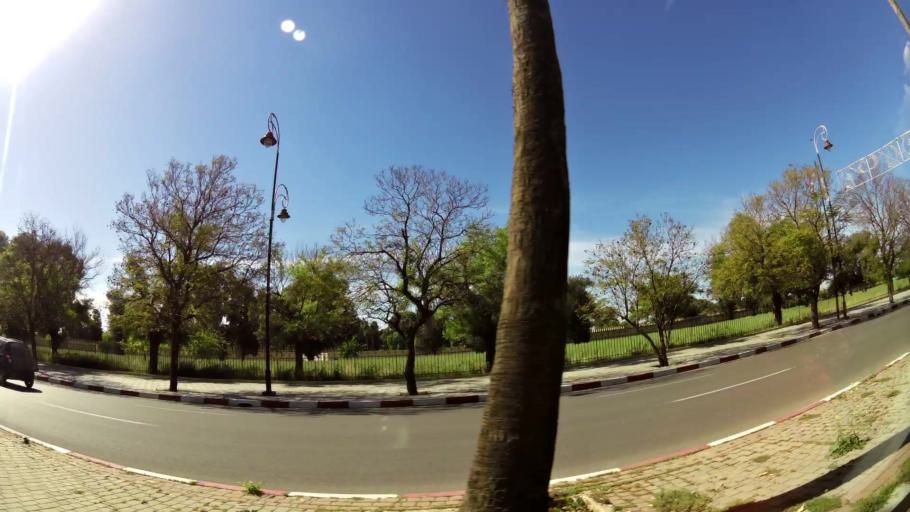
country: MA
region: Fes-Boulemane
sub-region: Fes
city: Fes
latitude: 34.0586
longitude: -5.0023
